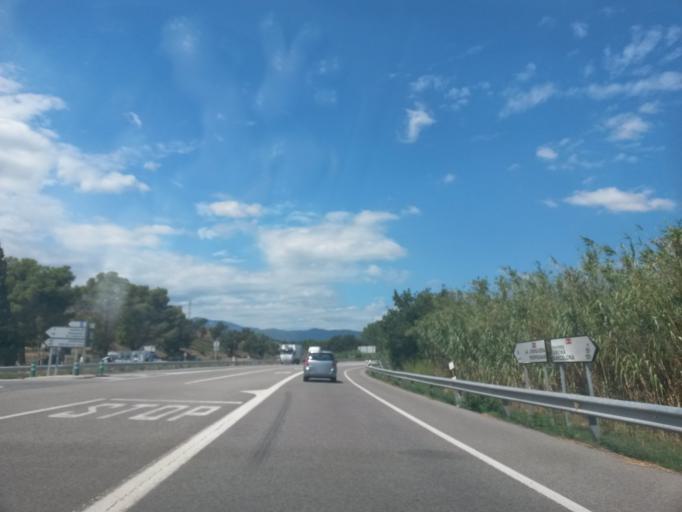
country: ES
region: Catalonia
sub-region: Provincia de Girona
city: Biure
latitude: 42.3508
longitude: 2.9068
